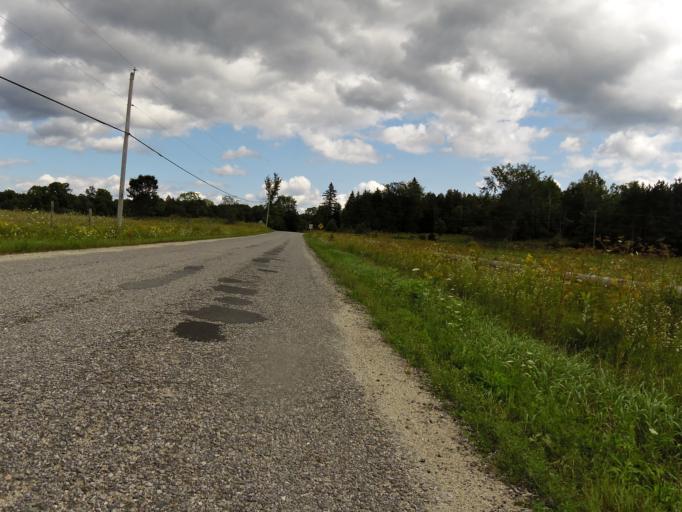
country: CA
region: Quebec
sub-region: Outaouais
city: Wakefield
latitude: 45.8084
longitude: -76.0069
